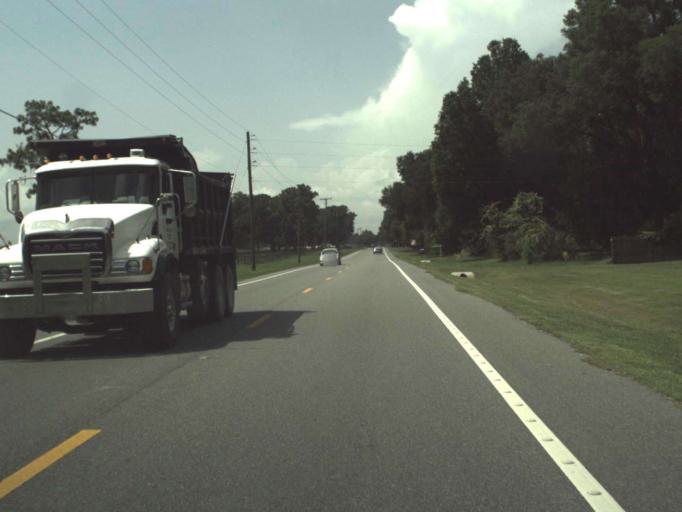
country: US
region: Florida
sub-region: Sumter County
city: Bushnell
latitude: 28.6828
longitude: -82.1043
